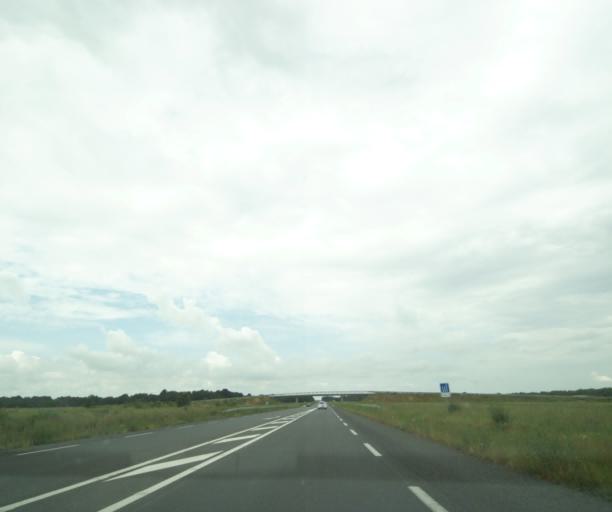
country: FR
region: Poitou-Charentes
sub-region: Departement des Deux-Sevres
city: Sainte-Verge
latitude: 47.0268
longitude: -0.2022
